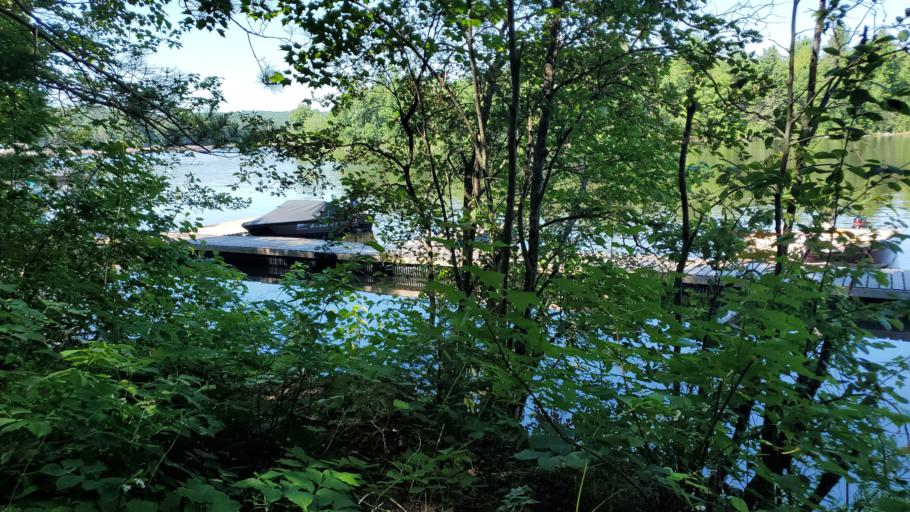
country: CA
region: Ontario
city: Mattawa
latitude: 46.2585
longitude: -78.2762
